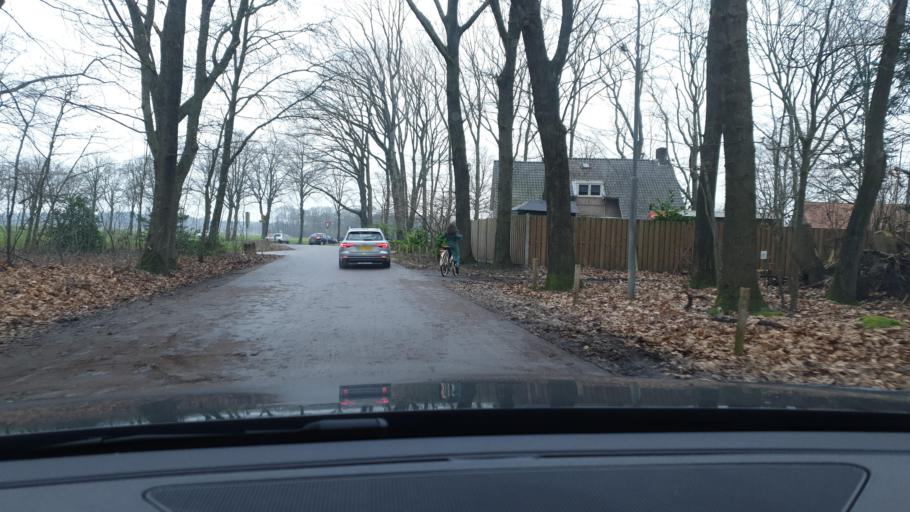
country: NL
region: North Brabant
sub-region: Gemeente Veldhoven
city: Oerle
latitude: 51.3977
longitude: 5.3755
